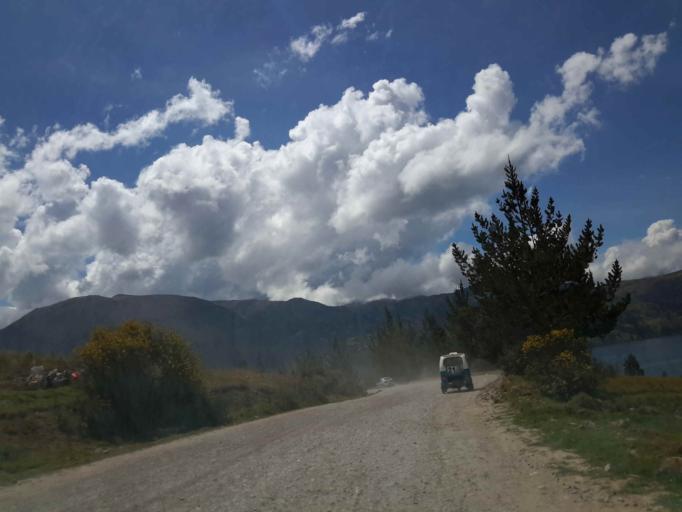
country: PE
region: Apurimac
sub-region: Provincia de Andahuaylas
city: Pacucha
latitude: -13.6213
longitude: -73.3372
